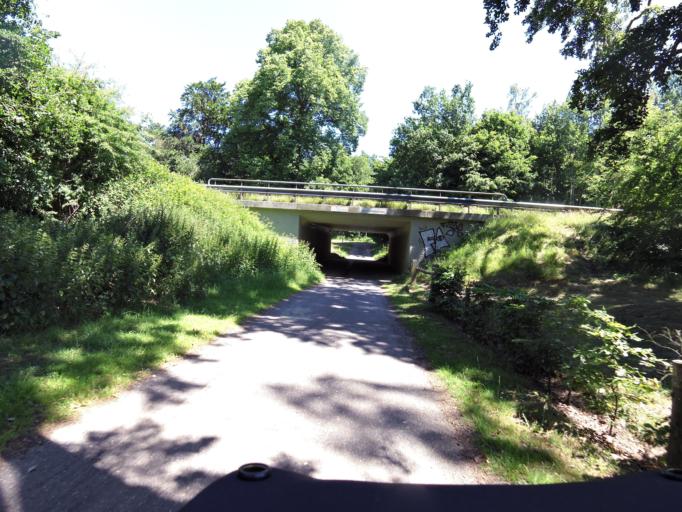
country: NL
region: Overijssel
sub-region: Gemeente Twenterand
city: Den Ham
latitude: 52.4906
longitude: 6.4244
